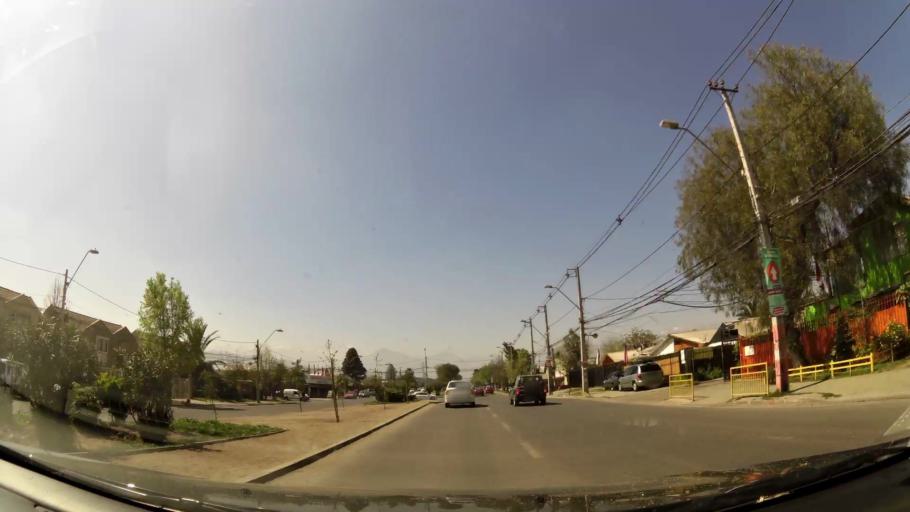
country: CL
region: Santiago Metropolitan
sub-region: Provincia de Santiago
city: Lo Prado
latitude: -33.3579
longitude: -70.7348
